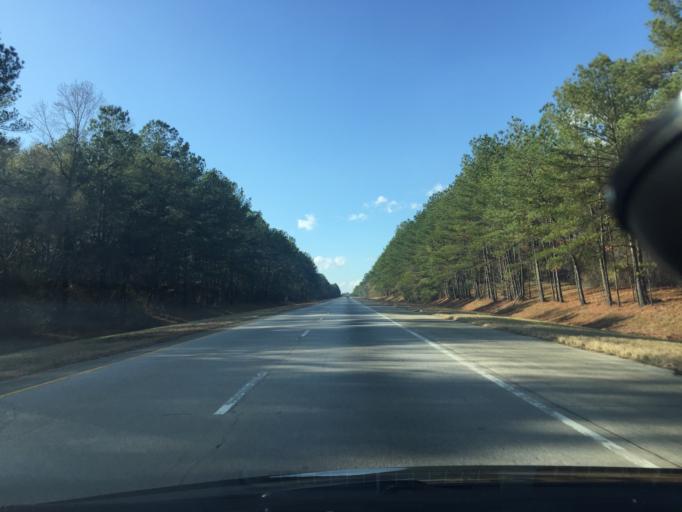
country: US
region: Georgia
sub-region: Treutlen County
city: Soperton
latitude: 32.4301
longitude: -82.4826
